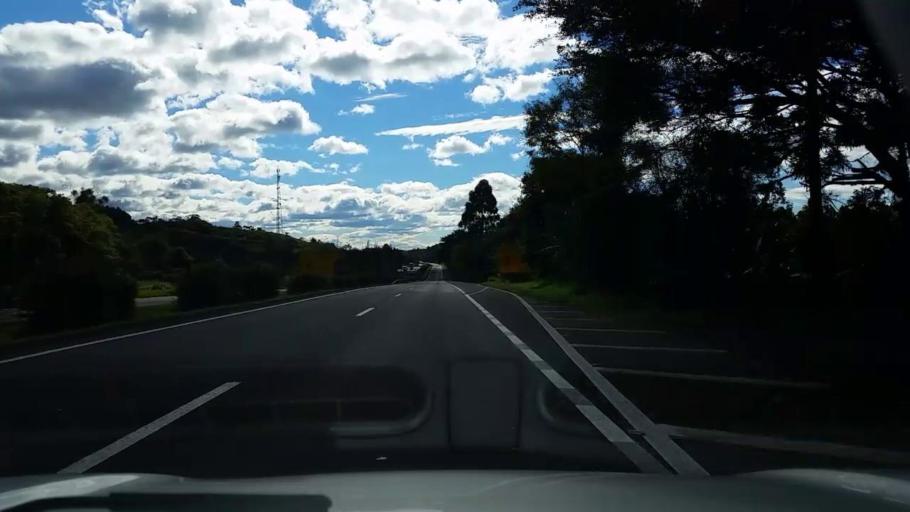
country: BR
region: Rio Grande do Sul
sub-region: Capao Da Canoa
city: Capao da Canoa
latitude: -29.6499
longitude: -50.1164
